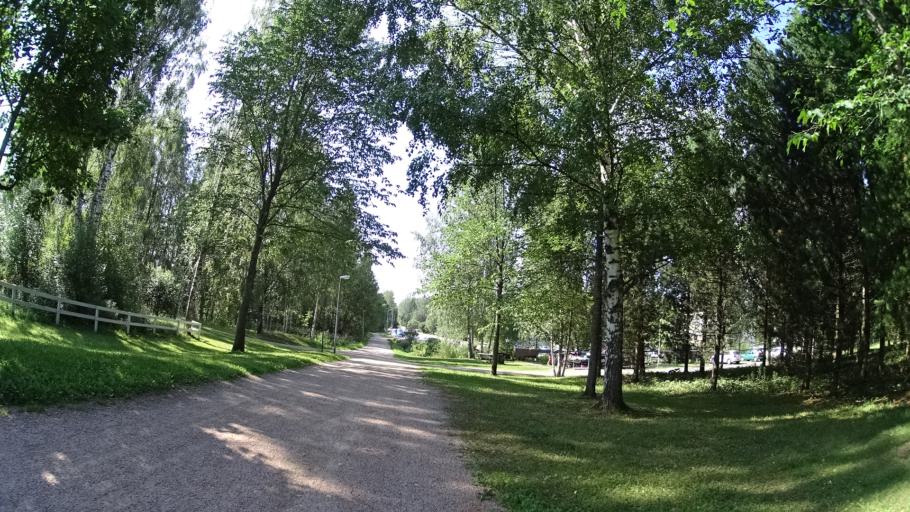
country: FI
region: Uusimaa
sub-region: Helsinki
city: Teekkarikylae
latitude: 60.2734
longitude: 24.8619
